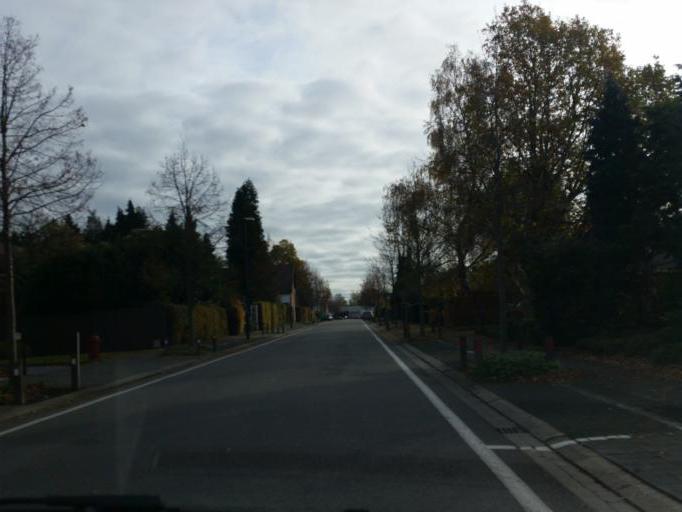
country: BE
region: Flanders
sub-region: Provincie Antwerpen
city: Kontich
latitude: 51.1426
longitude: 4.4531
